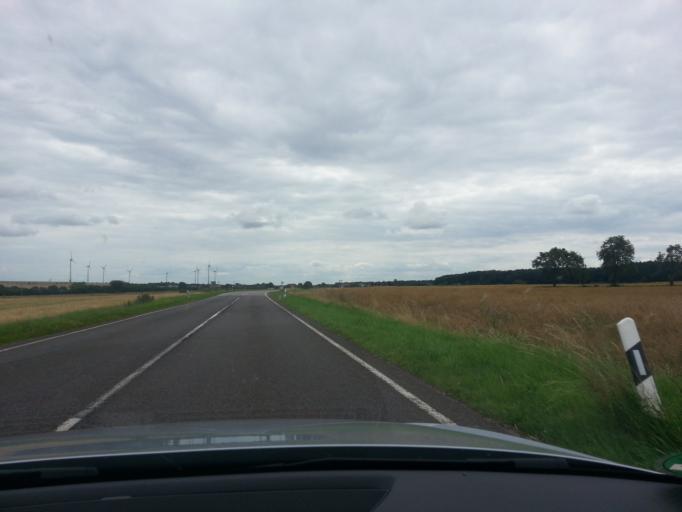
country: DE
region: Saarland
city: Orscholz
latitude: 49.4796
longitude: 6.4696
